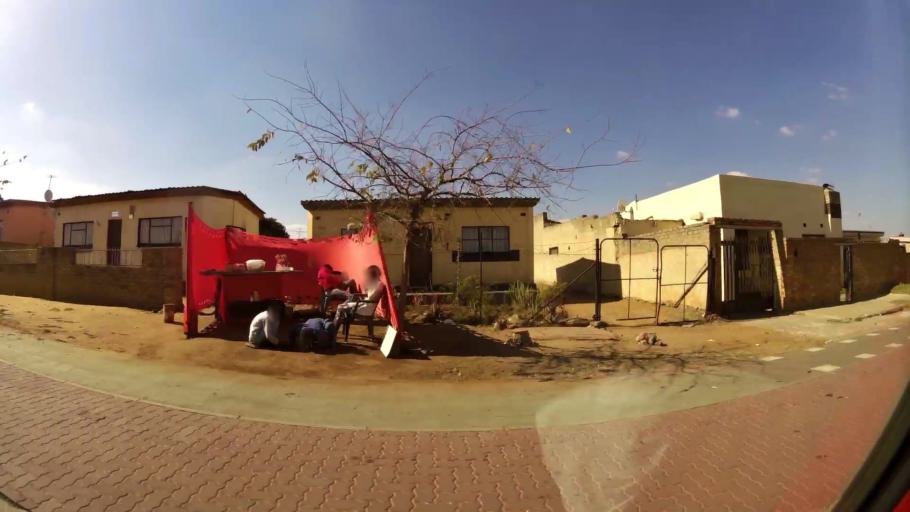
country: ZA
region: Gauteng
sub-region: City of Johannesburg Metropolitan Municipality
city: Soweto
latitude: -26.2420
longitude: 27.8944
